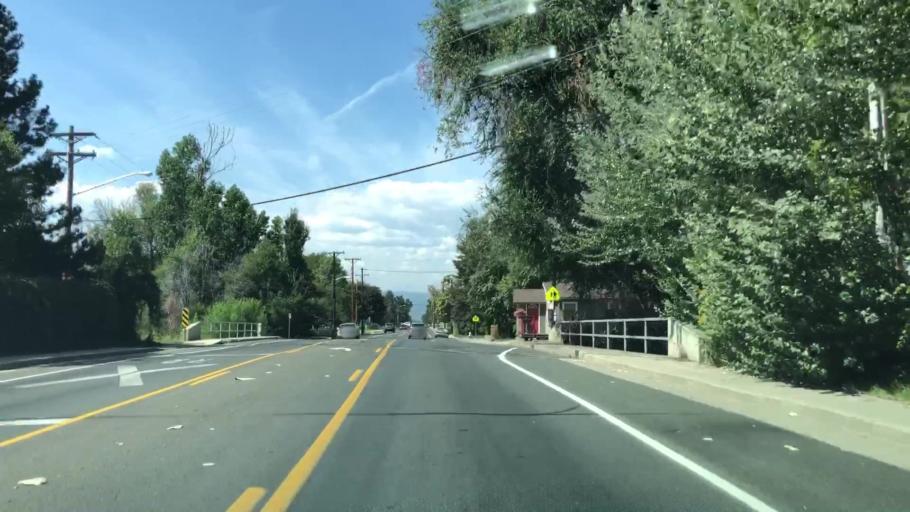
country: US
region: Colorado
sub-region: Larimer County
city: Loveland
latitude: 40.3928
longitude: -105.0769
